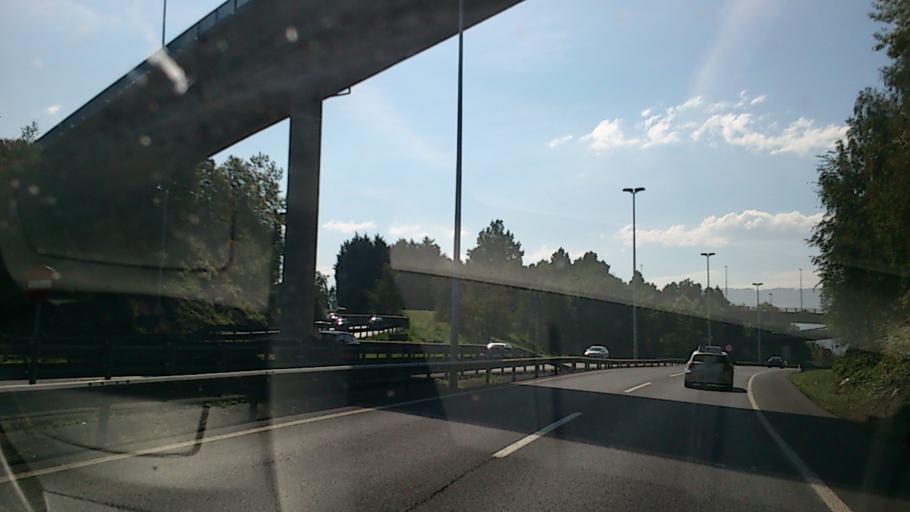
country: ES
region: Basque Country
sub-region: Bizkaia
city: Erandio
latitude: 43.3040
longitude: -2.9614
